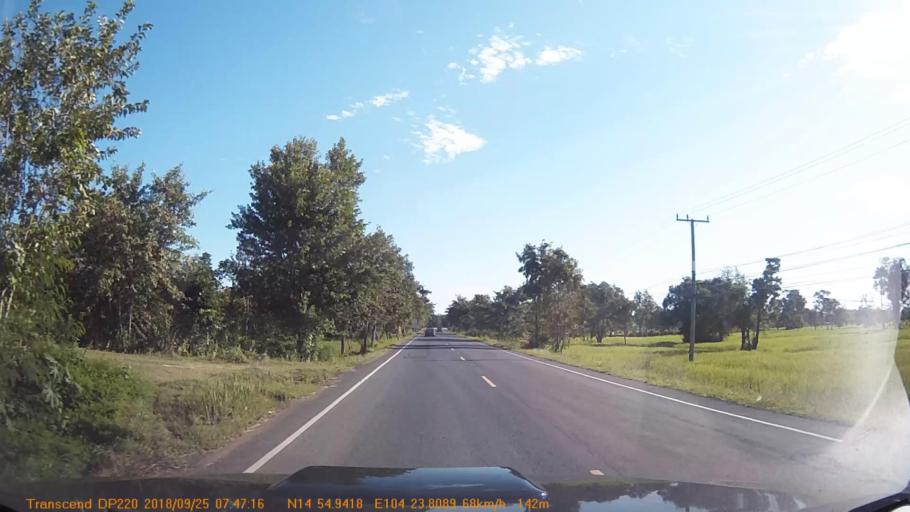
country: TH
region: Sisaket
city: Phayu
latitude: 14.9159
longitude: 104.3969
